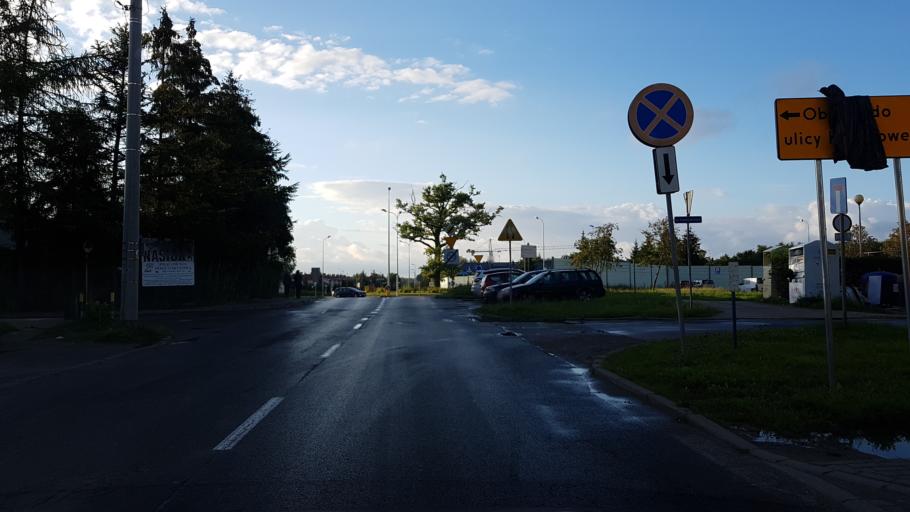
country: PL
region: West Pomeranian Voivodeship
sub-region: Koszalin
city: Koszalin
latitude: 54.2072
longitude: 16.1613
